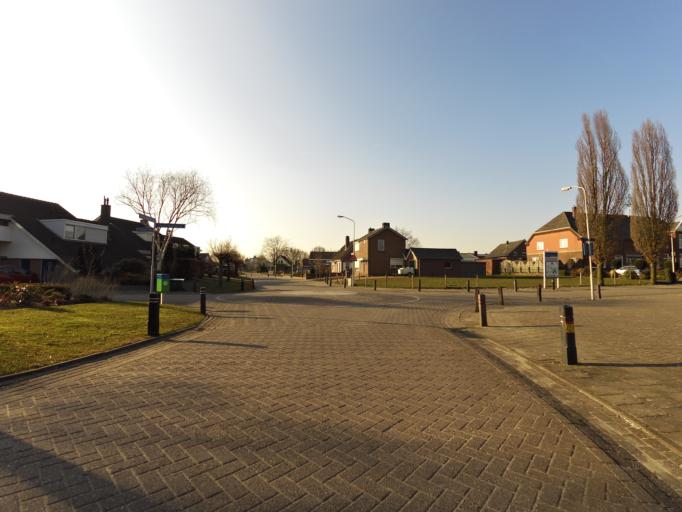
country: NL
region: Gelderland
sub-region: Gemeente Montferland
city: s-Heerenberg
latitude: 51.8859
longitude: 6.3045
